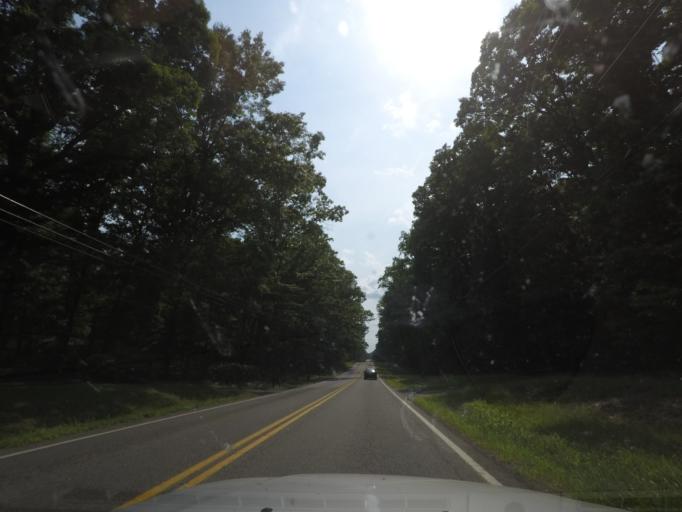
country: US
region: Virginia
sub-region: Fluvanna County
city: Weber City
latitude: 37.7802
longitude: -78.2393
